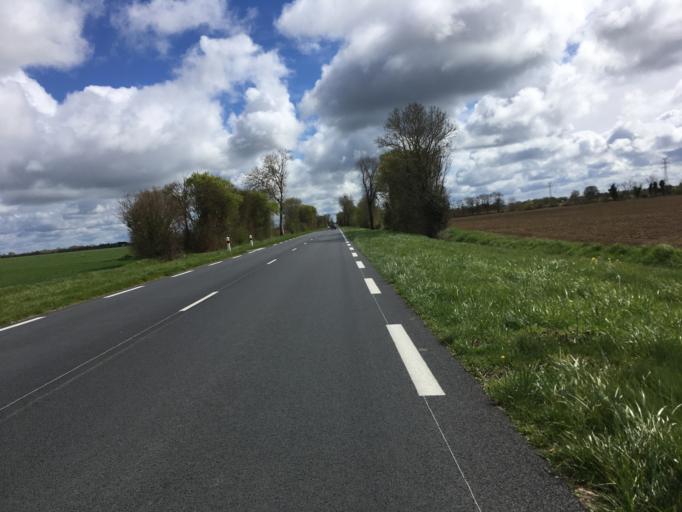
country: FR
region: Poitou-Charentes
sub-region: Departement de la Charente-Maritime
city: Thaire
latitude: 46.1048
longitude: -0.9692
